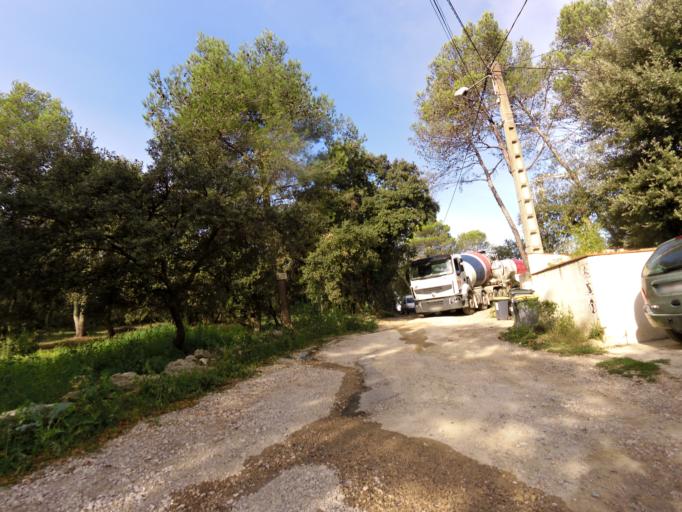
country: FR
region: Languedoc-Roussillon
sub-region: Departement du Gard
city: Aigues-Vives
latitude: 43.7426
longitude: 4.1643
